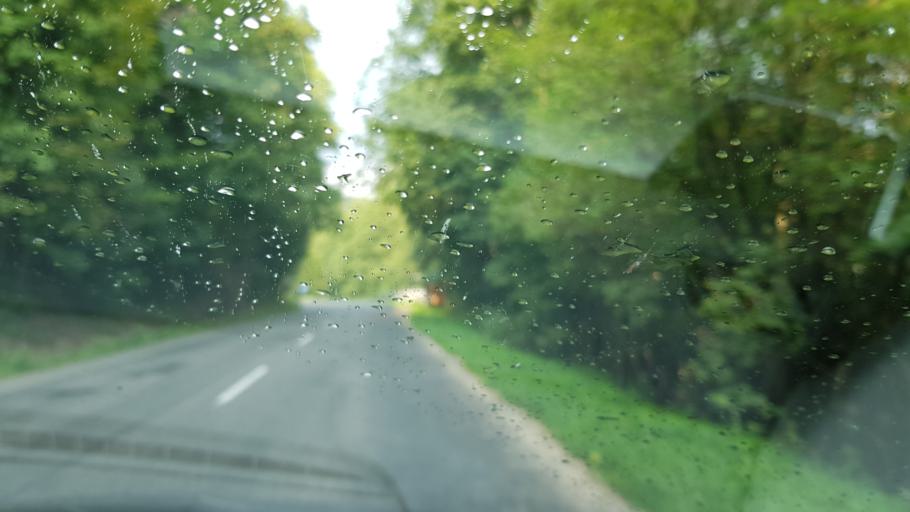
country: CZ
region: Olomoucky
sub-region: Okres Sumperk
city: Hanusovice
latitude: 50.0936
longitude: 16.8529
